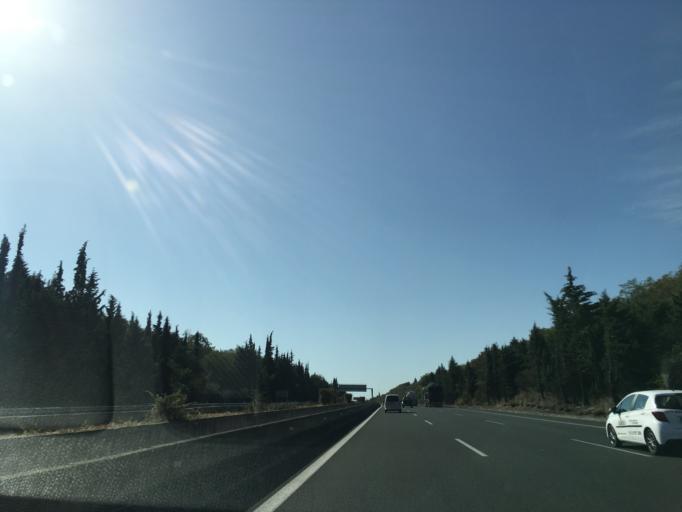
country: GR
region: Central Macedonia
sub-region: Nomos Pierias
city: Makrygialos
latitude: 40.4537
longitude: 22.5797
